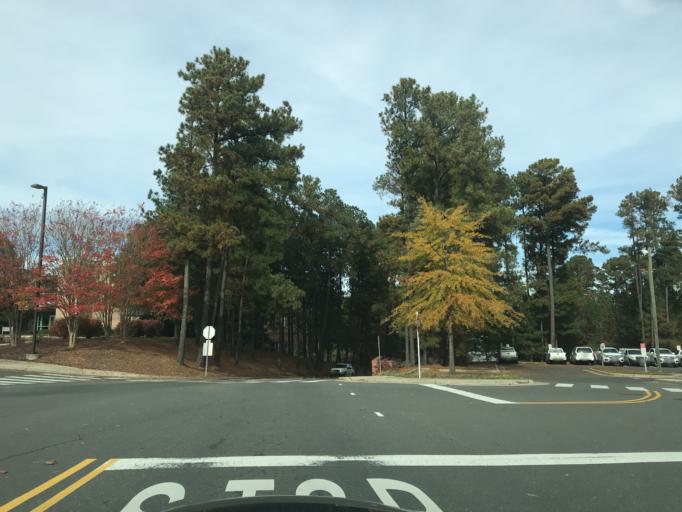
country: US
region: North Carolina
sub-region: Wake County
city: West Raleigh
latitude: 35.7856
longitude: -78.6816
